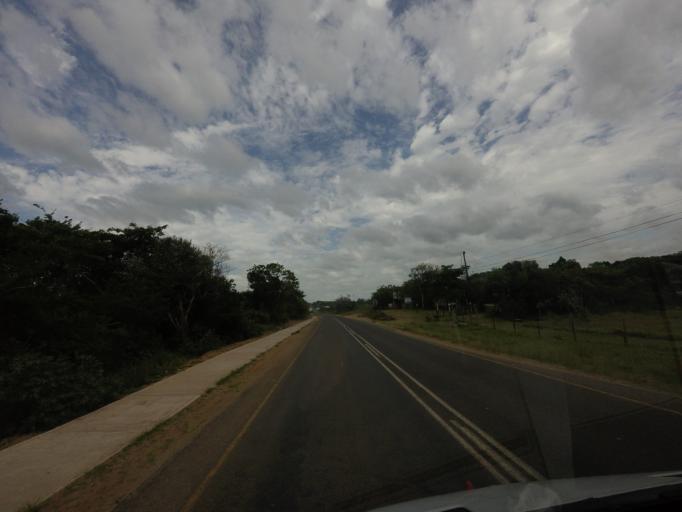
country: ZA
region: KwaZulu-Natal
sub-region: uMkhanyakude District Municipality
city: Mtubatuba
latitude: -28.3760
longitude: 32.3762
